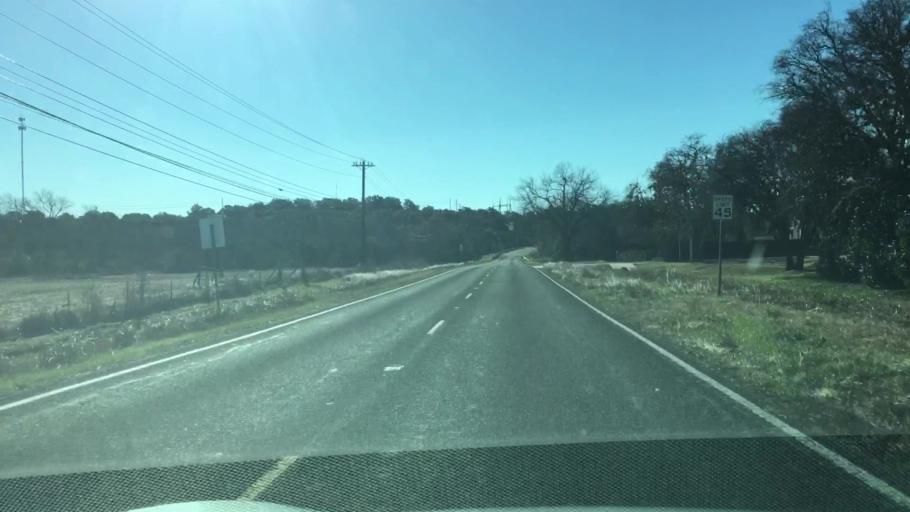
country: US
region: Texas
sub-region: Blanco County
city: Blanco
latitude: 30.0888
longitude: -98.4148
